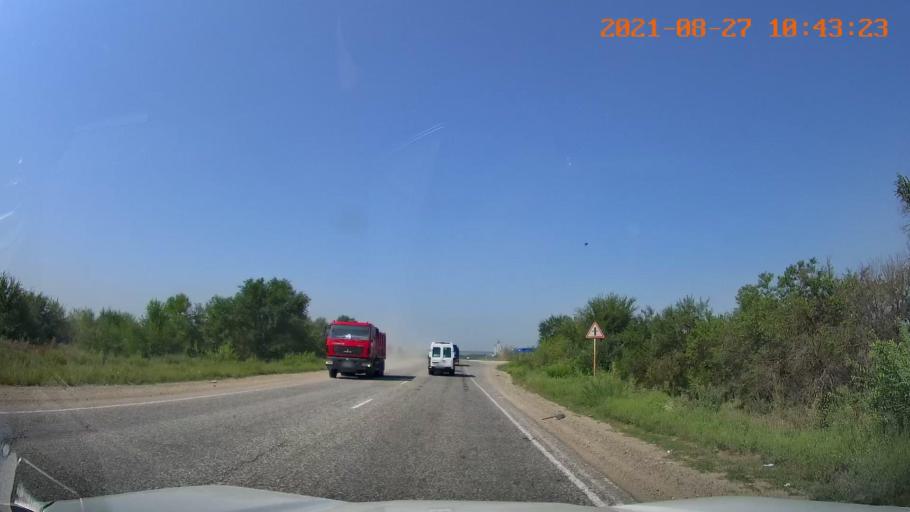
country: RU
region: Karachayevo-Cherkesiya
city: Psyzh
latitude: 44.3007
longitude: 42.0311
